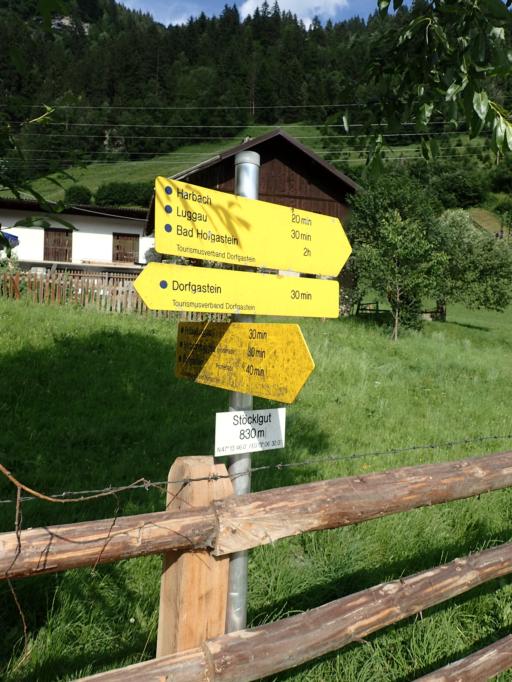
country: AT
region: Salzburg
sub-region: Politischer Bezirk Sankt Johann im Pongau
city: Dorfgastein
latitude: 47.2263
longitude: 13.1092
